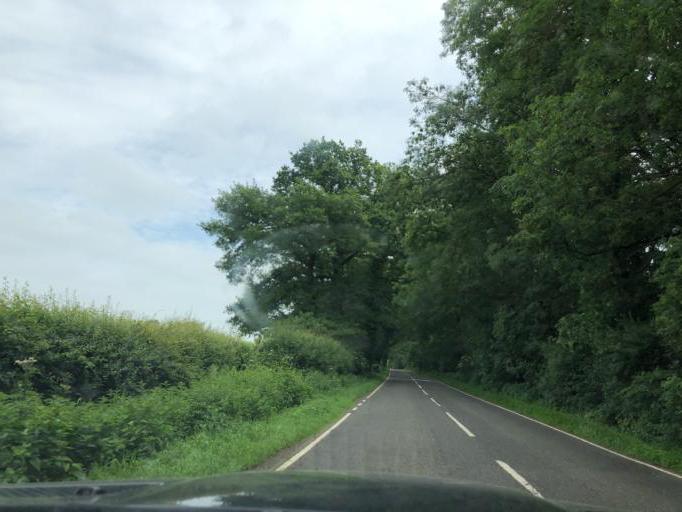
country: GB
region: England
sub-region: Warwickshire
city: Kenilworth
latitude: 52.3250
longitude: -1.6034
